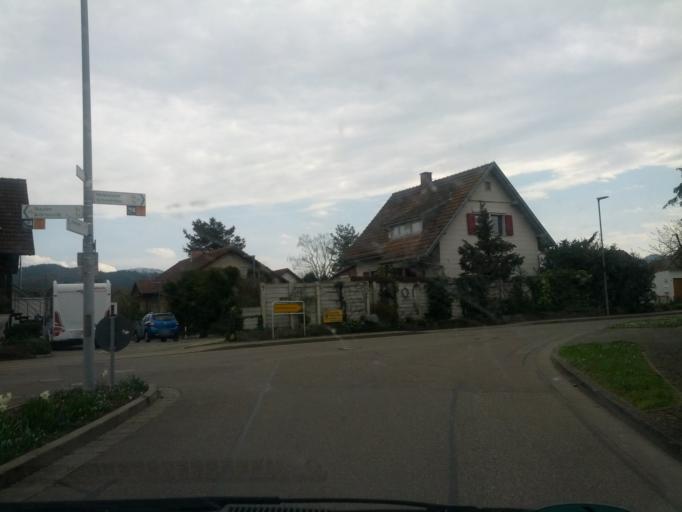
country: DE
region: Baden-Wuerttemberg
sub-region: Freiburg Region
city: Bad Krozingen
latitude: 47.9057
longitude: 7.7044
